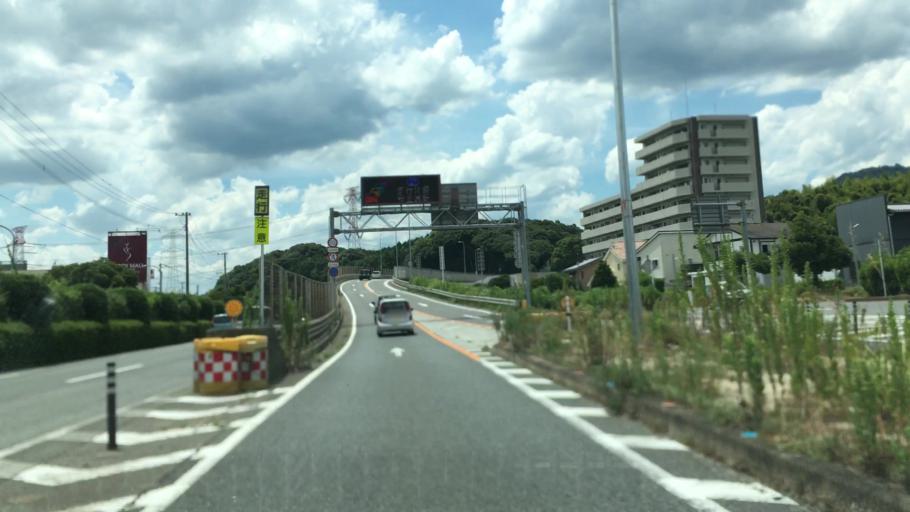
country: JP
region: Fukuoka
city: Chikushino-shi
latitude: 33.4459
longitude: 130.5388
